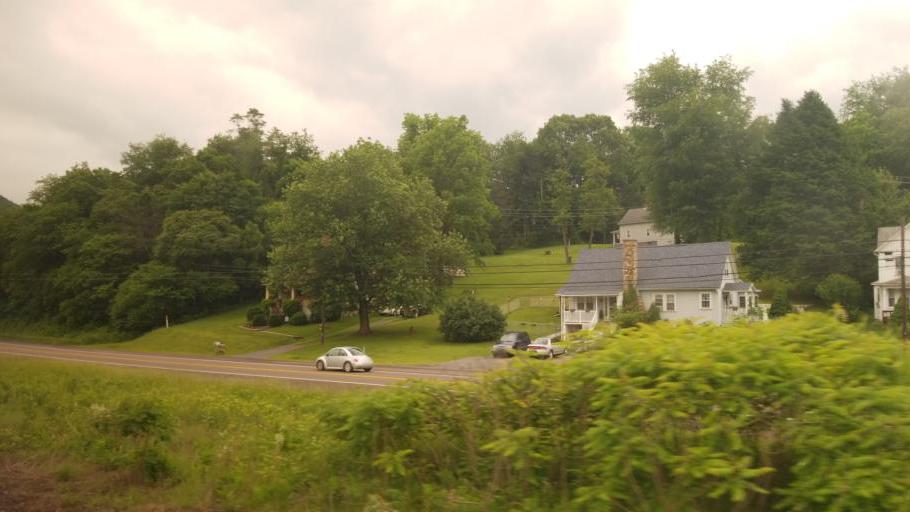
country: US
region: Maryland
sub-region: Allegany County
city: Cumberland
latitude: 39.6892
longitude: -78.7825
